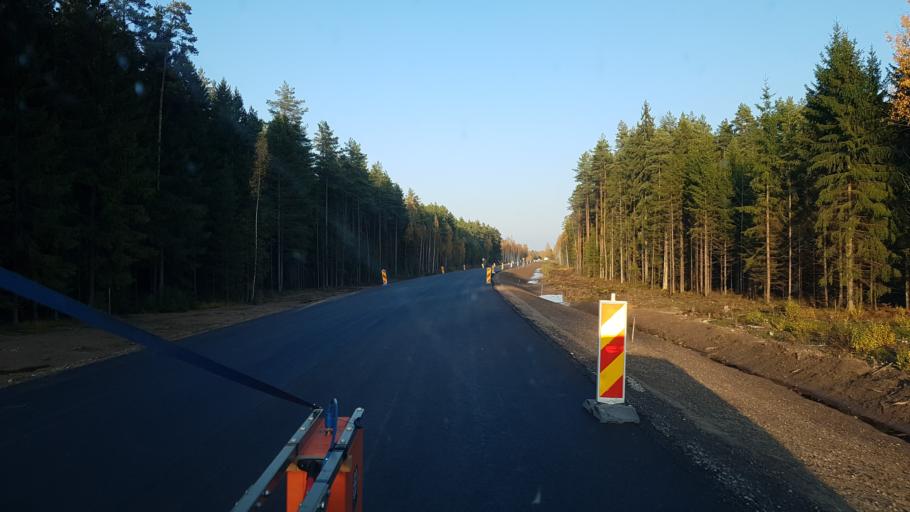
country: EE
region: Polvamaa
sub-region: Polva linn
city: Polva
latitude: 57.9353
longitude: 27.1897
